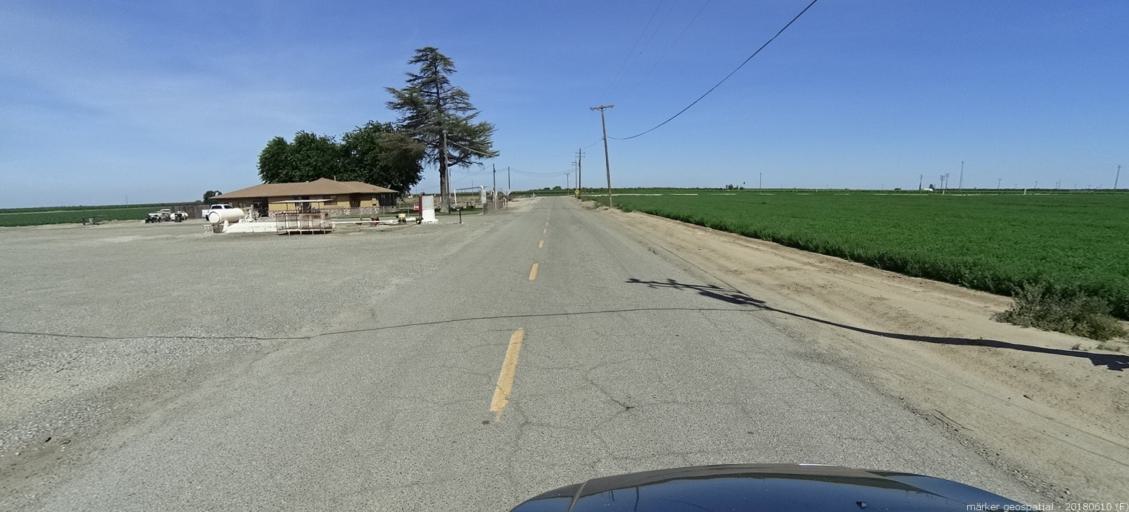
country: US
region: California
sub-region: Madera County
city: Chowchilla
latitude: 37.0240
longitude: -120.3500
